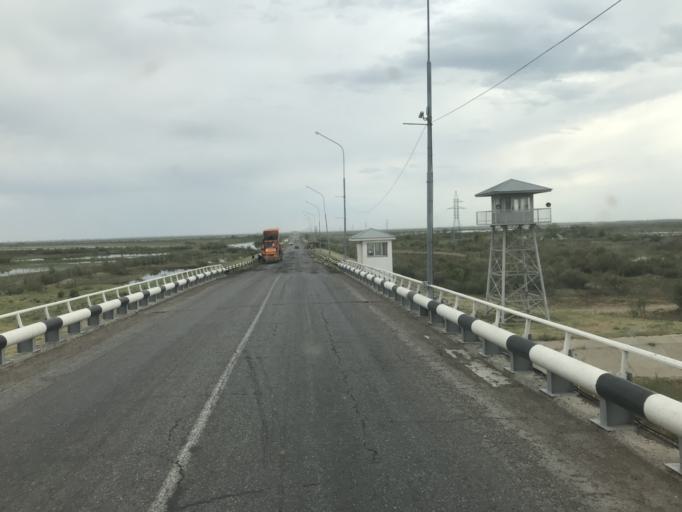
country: KZ
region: Ongtustik Qazaqstan
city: Ilyich
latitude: 41.0285
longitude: 68.5162
